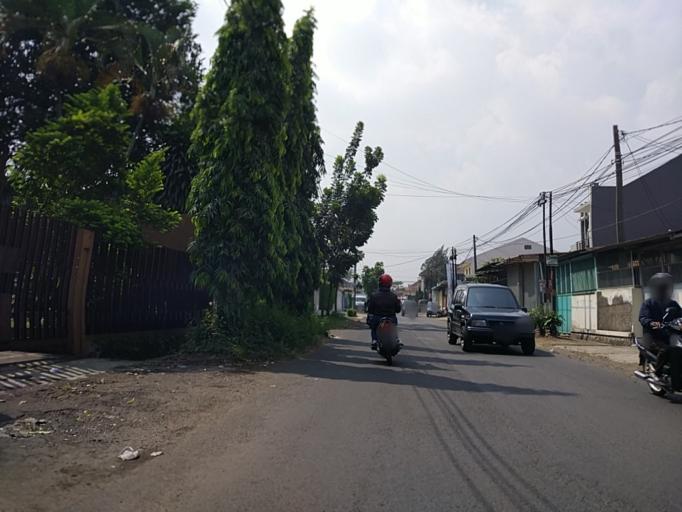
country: ID
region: West Java
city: Margahayukencana
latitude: -6.9330
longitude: 107.5732
